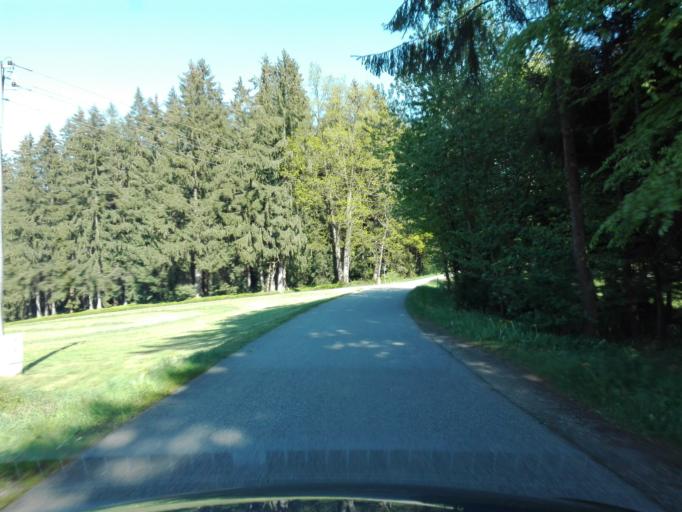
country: AT
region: Upper Austria
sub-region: Politischer Bezirk Rohrbach
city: Pfarrkirchen im Muehlkreis
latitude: 48.4242
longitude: 13.7240
